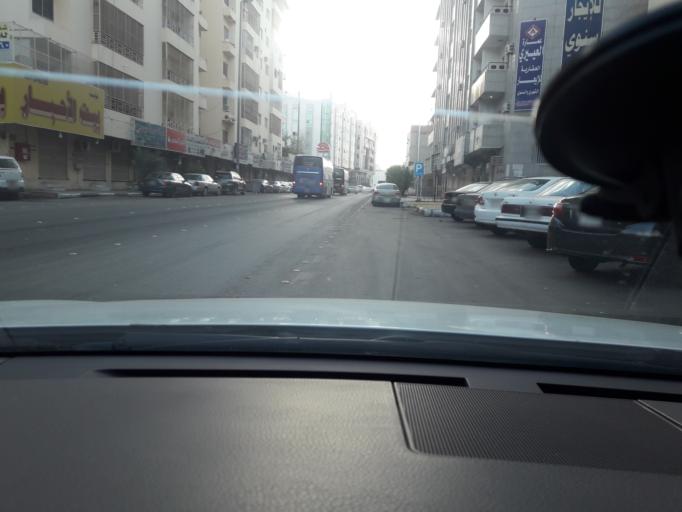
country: SA
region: Al Madinah al Munawwarah
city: Medina
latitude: 24.4557
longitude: 39.6169
